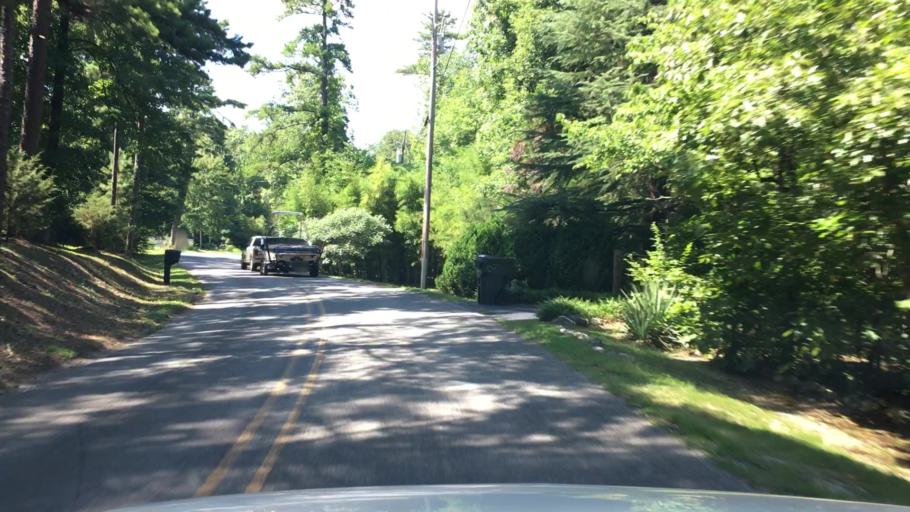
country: US
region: Arkansas
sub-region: Garland County
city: Piney
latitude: 34.5305
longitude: -93.3368
